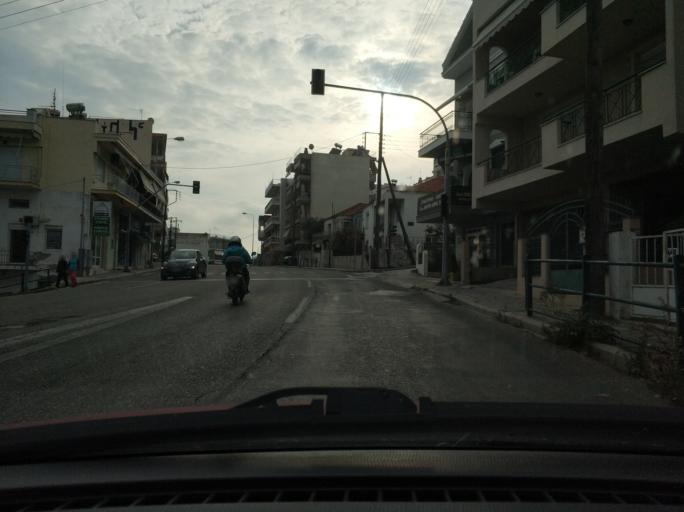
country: GR
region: East Macedonia and Thrace
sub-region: Nomos Kavalas
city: Kavala
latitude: 40.9248
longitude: 24.3895
